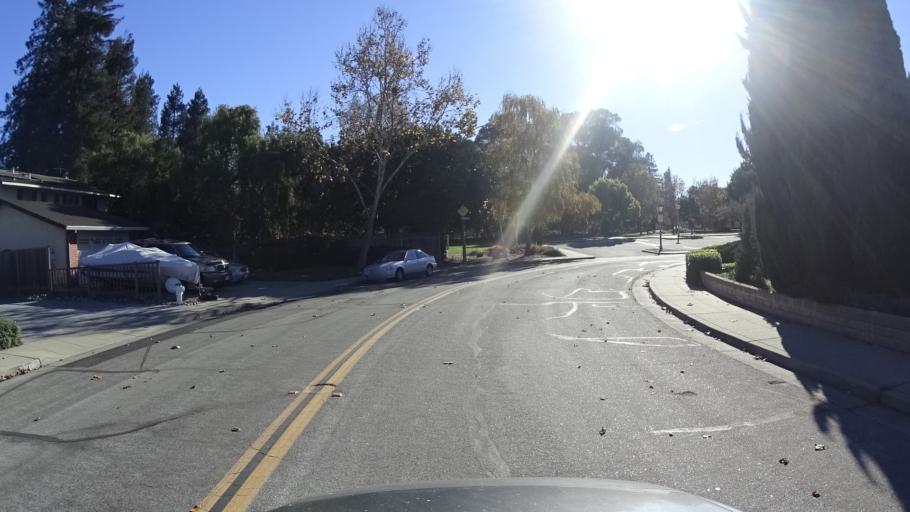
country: US
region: California
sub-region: Santa Clara County
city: Cupertino
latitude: 37.3434
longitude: -122.0238
